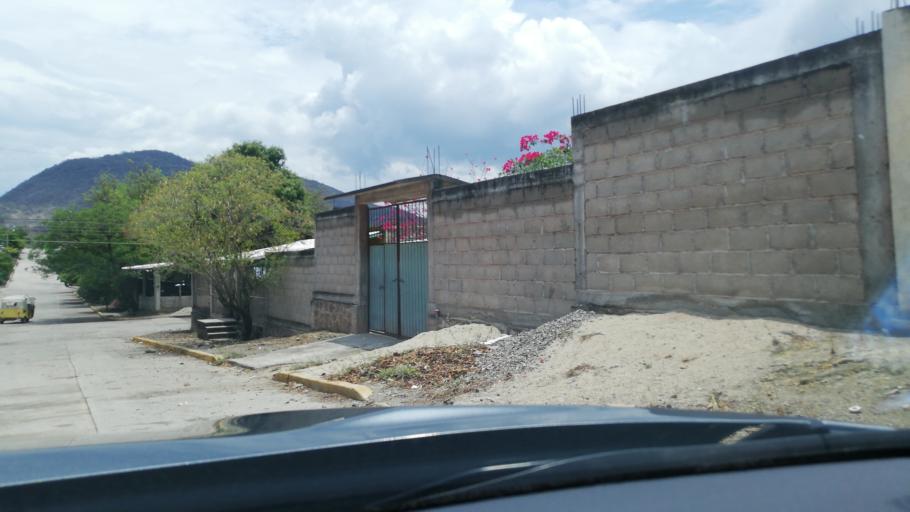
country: MX
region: Oaxaca
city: Santa Maria Jalapa del Marques
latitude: 16.4424
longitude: -95.4404
